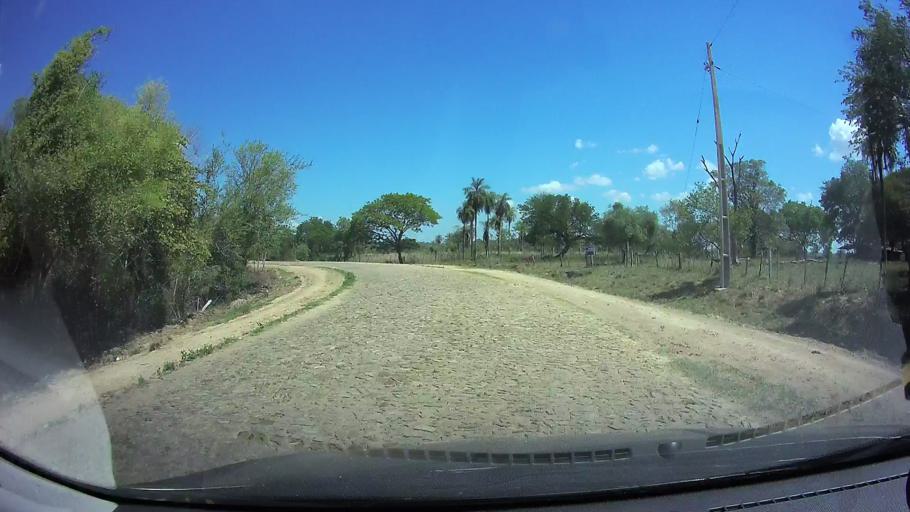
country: PY
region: Cordillera
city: Emboscada
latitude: -25.1274
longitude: -57.2685
